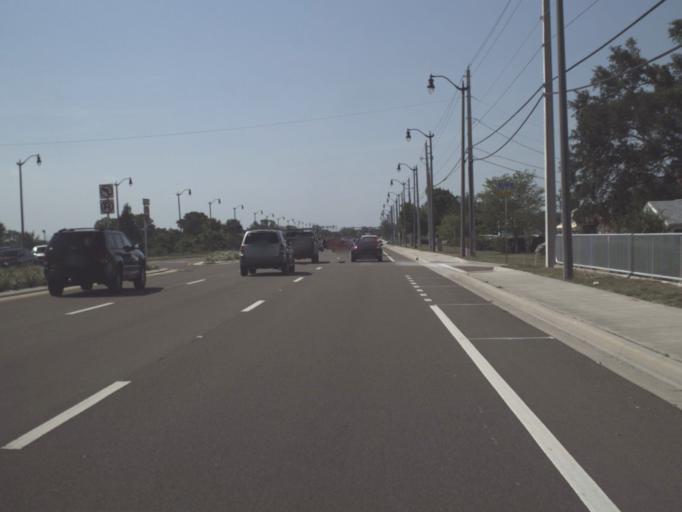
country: US
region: Florida
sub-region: Brevard County
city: Rockledge
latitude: 28.3257
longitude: -80.7181
